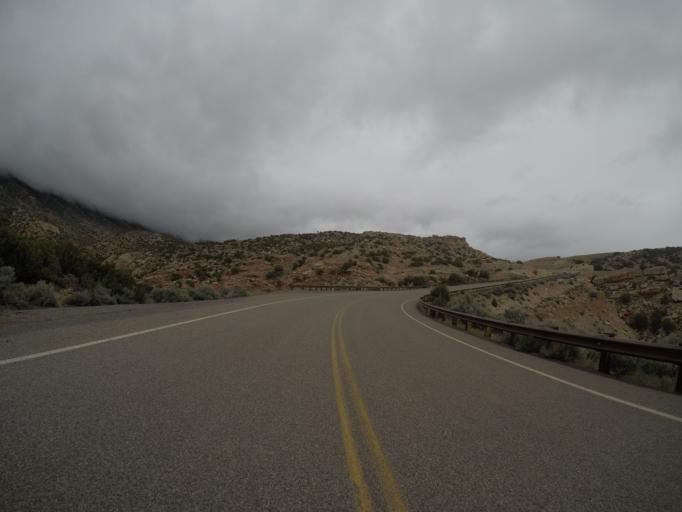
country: US
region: Wyoming
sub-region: Big Horn County
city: Lovell
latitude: 45.0460
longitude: -108.2536
